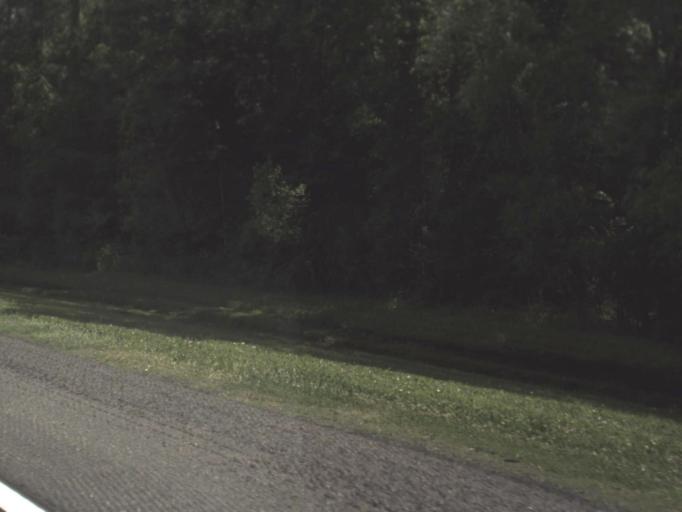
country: US
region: Florida
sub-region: Nassau County
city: Yulee
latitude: 30.4963
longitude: -81.6390
